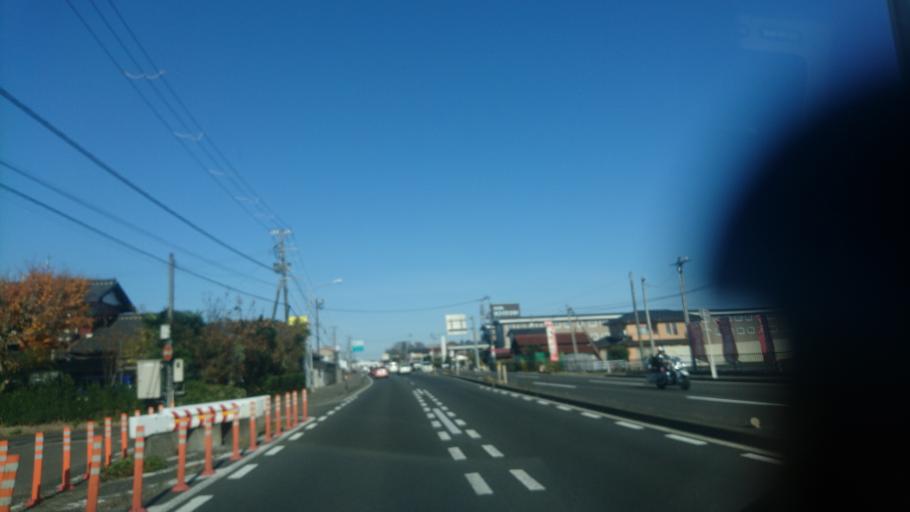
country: JP
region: Miyagi
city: Iwanuma
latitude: 38.1252
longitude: 140.8732
